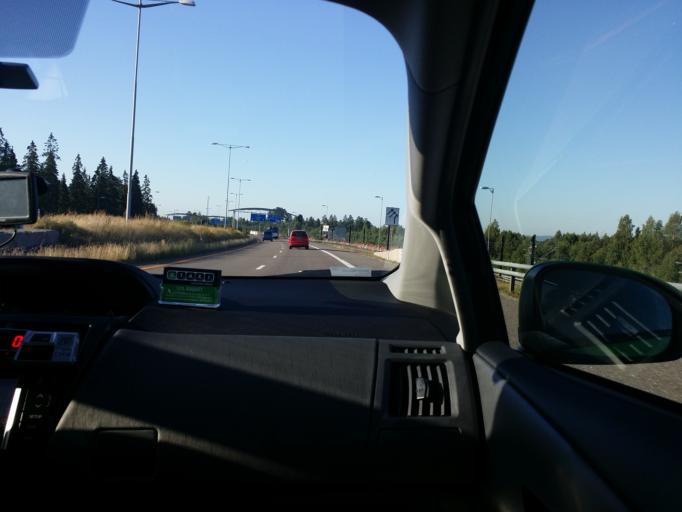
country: NO
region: Akershus
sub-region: Nannestad
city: Teigebyen
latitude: 60.1846
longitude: 11.0933
